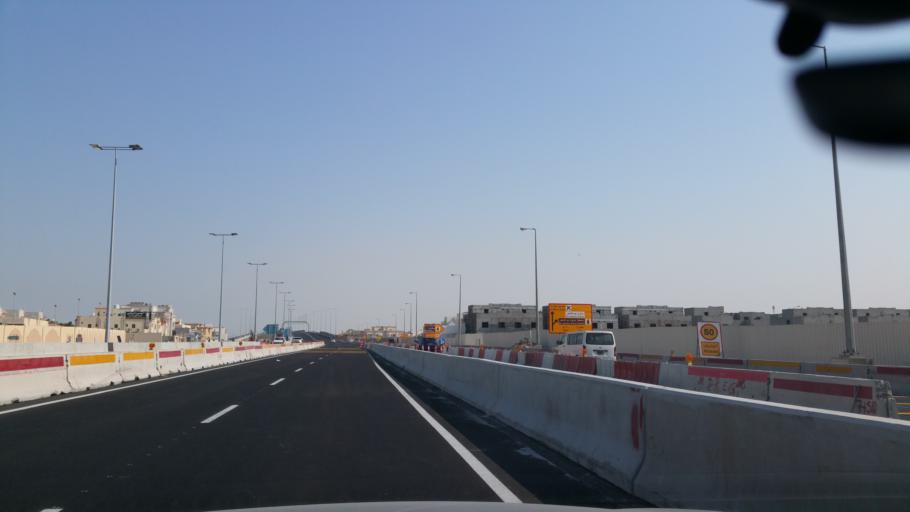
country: QA
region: Baladiyat ad Dawhah
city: Doha
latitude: 25.2440
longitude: 51.4935
